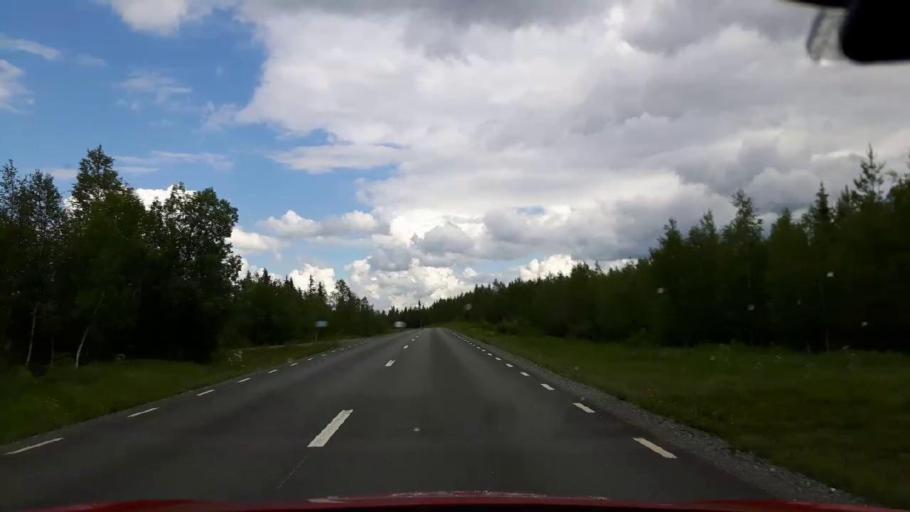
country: SE
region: Jaemtland
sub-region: Krokoms Kommun
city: Krokom
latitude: 63.5940
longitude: 14.3035
